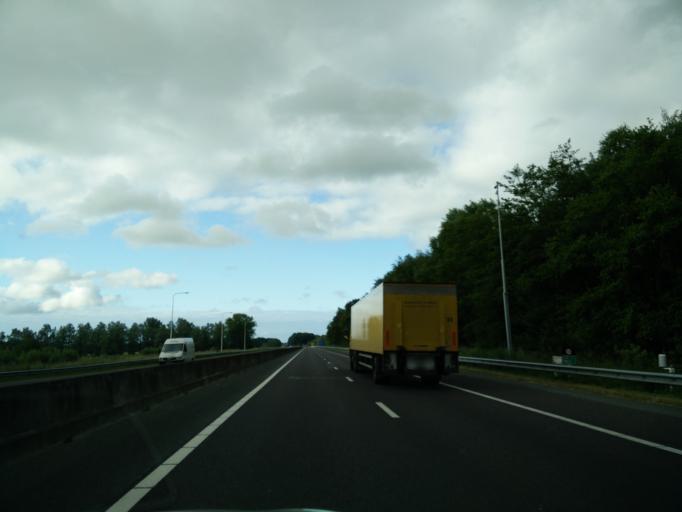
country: NL
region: Groningen
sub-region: Gemeente Haren
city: Haren
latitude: 53.1378
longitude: 6.6082
